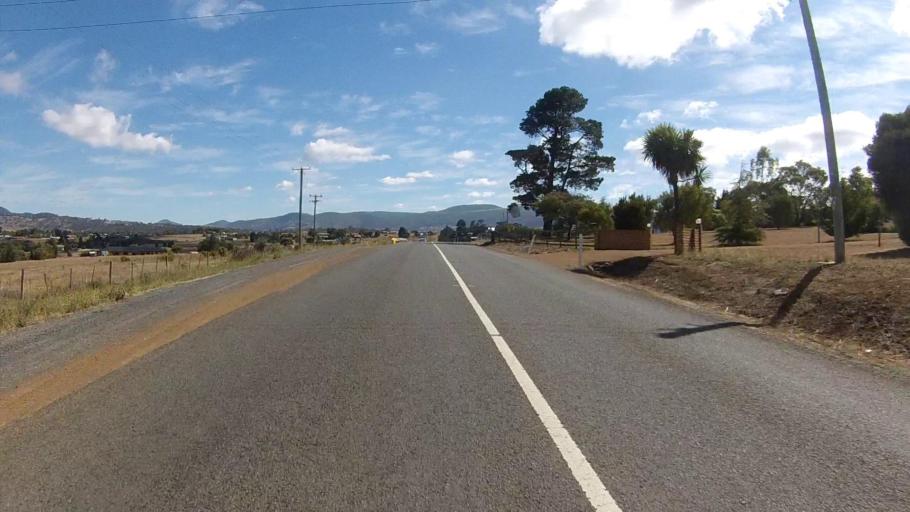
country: AU
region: Tasmania
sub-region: Brighton
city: Bridgewater
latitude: -42.7051
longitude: 147.2707
